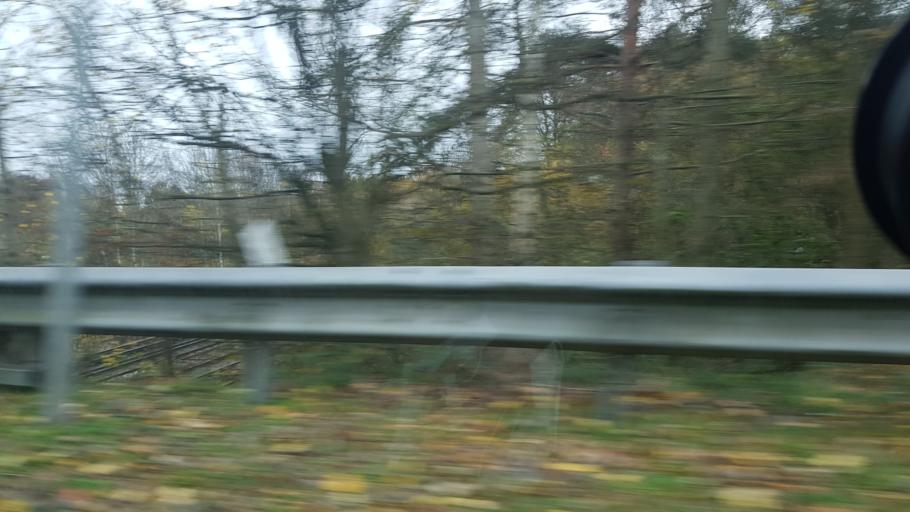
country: GB
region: England
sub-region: Hampshire
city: Fleet
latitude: 51.2928
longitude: -0.8024
